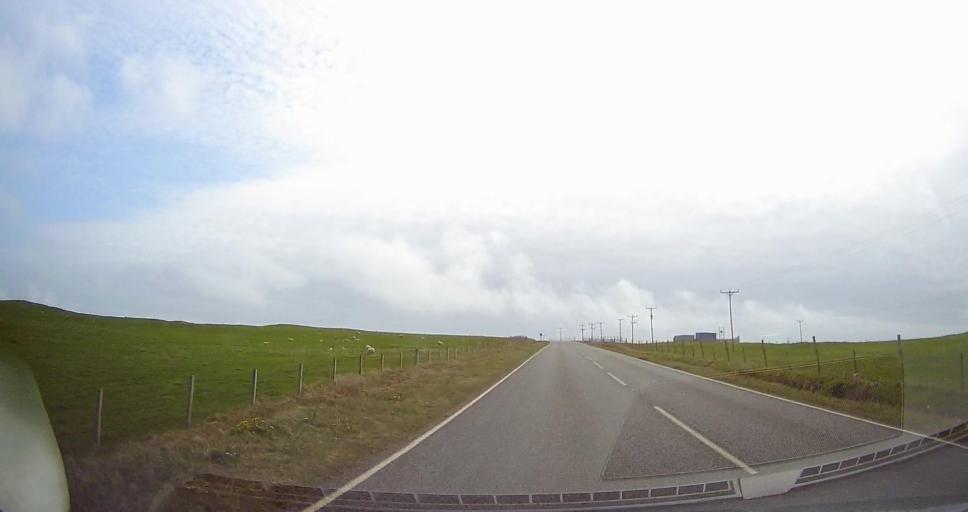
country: GB
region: Scotland
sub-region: Shetland Islands
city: Sandwick
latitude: 59.9005
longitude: -1.3032
